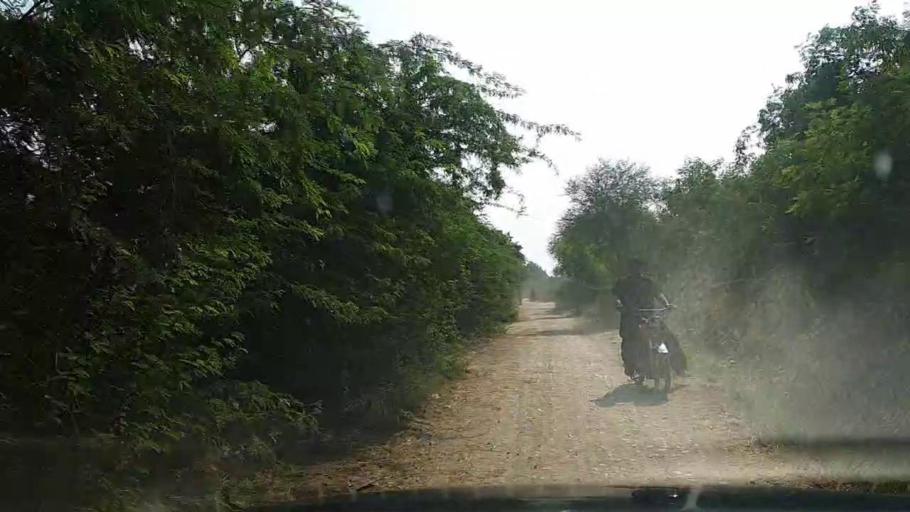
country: PK
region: Sindh
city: Mirpur Batoro
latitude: 24.6980
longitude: 68.2191
